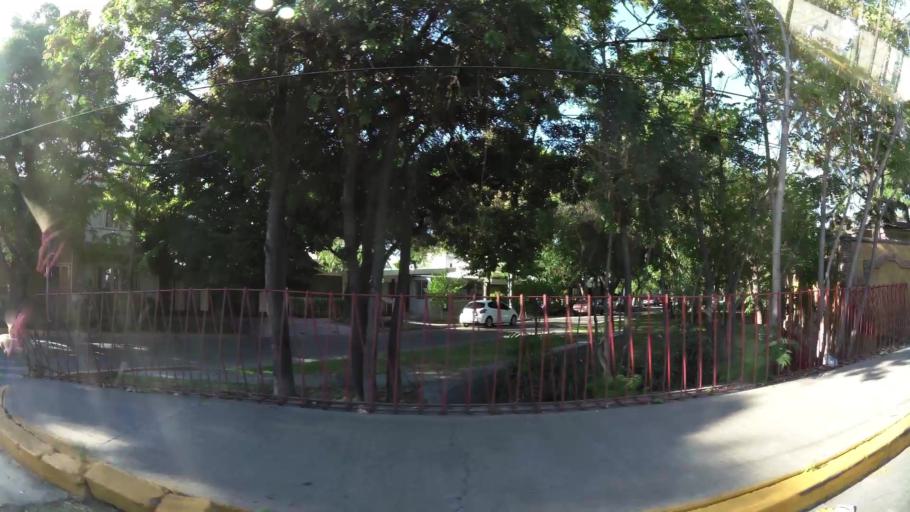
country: AR
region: Mendoza
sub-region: Departamento de Godoy Cruz
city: Godoy Cruz
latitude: -32.9126
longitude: -68.8397
